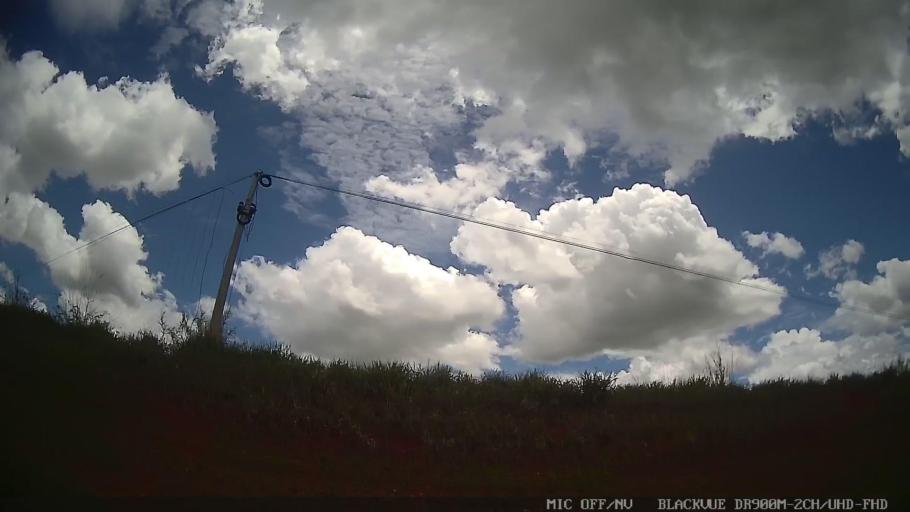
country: BR
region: Sao Paulo
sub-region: Jaguariuna
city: Jaguariuna
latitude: -22.7181
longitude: -46.9442
